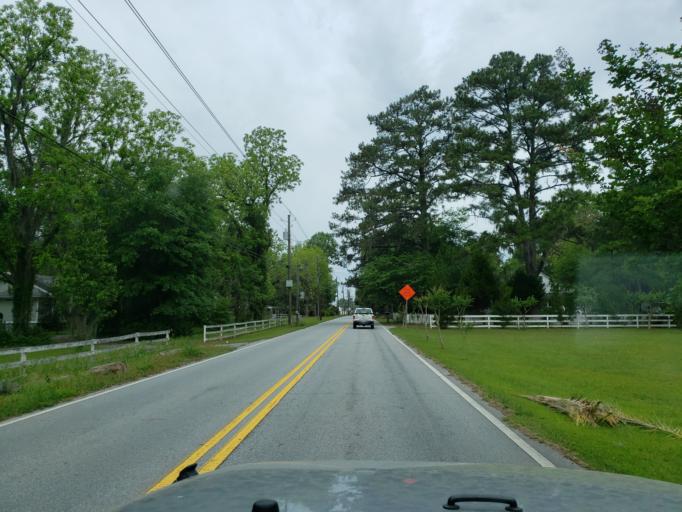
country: US
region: Georgia
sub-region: Chatham County
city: Port Wentworth
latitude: 32.1829
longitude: -81.2137
